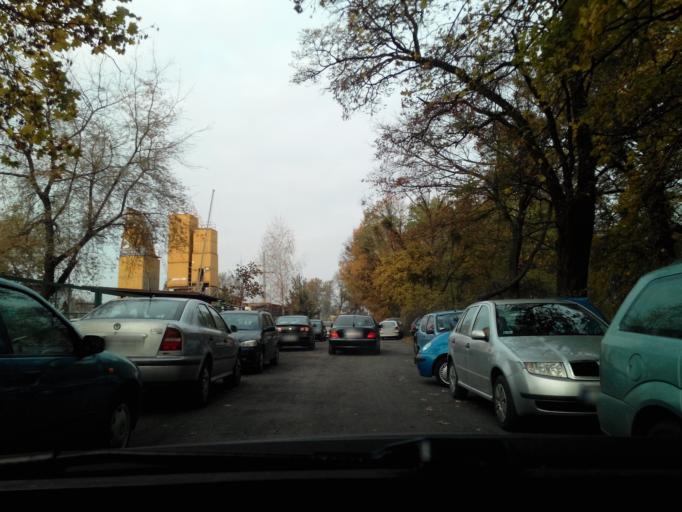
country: PL
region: Kujawsko-Pomorskie
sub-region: Powiat brodnicki
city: Brodnica
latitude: 53.2605
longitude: 19.3904
